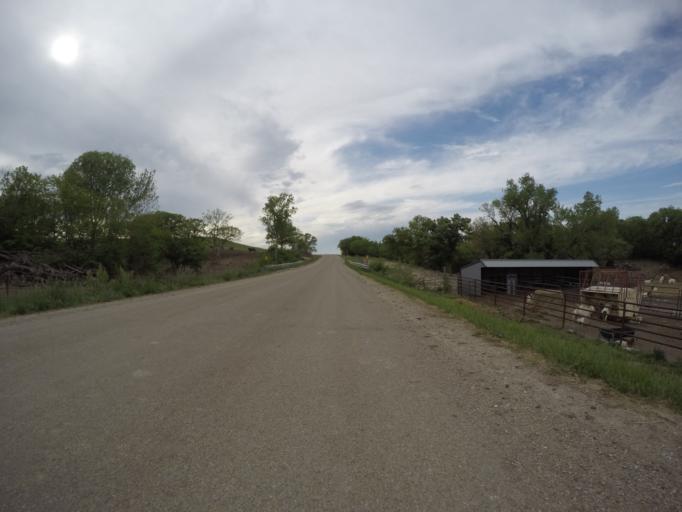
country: US
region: Kansas
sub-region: Riley County
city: Ogden
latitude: 39.0285
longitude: -96.6120
